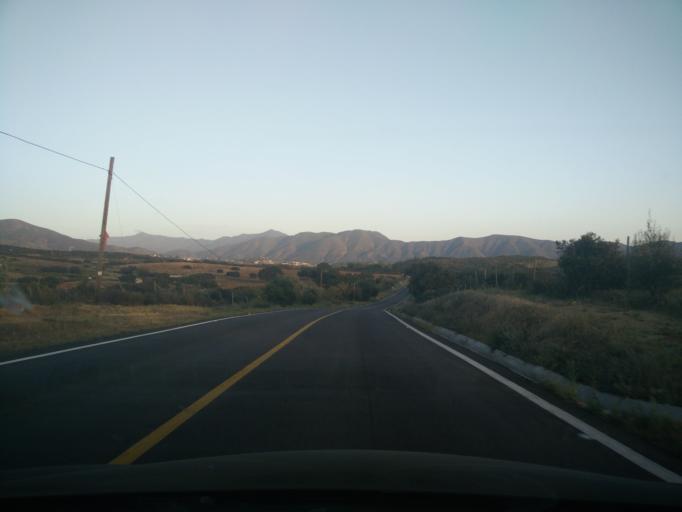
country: MX
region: Baja California
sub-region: Ensenada
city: Rancho Verde
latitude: 31.9974
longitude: -116.6584
